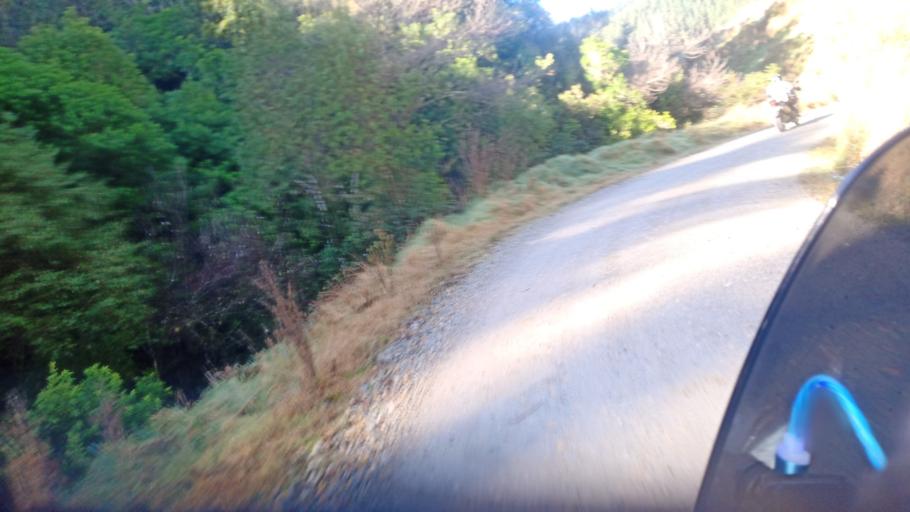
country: NZ
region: Hawke's Bay
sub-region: Wairoa District
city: Wairoa
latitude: -38.6617
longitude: 177.5041
